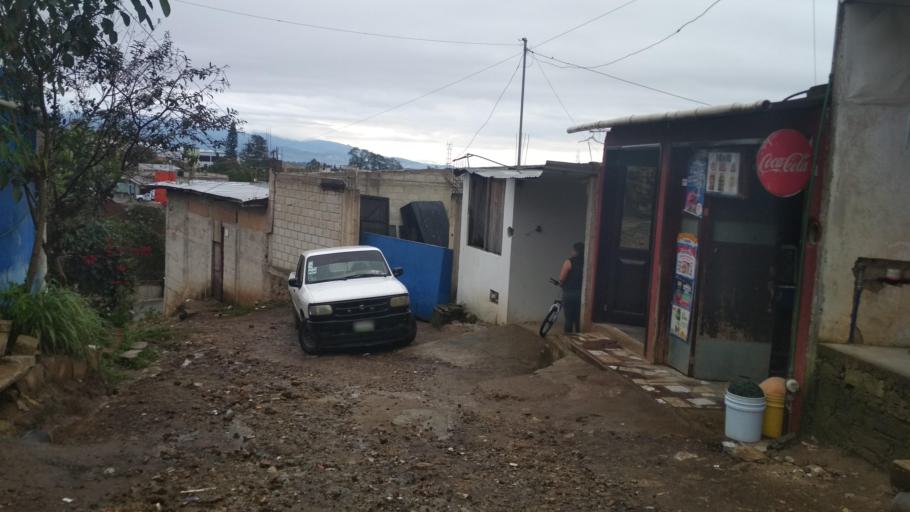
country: MX
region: Veracruz
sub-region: Emiliano Zapata
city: Las Trancas
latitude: 19.5055
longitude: -96.8684
